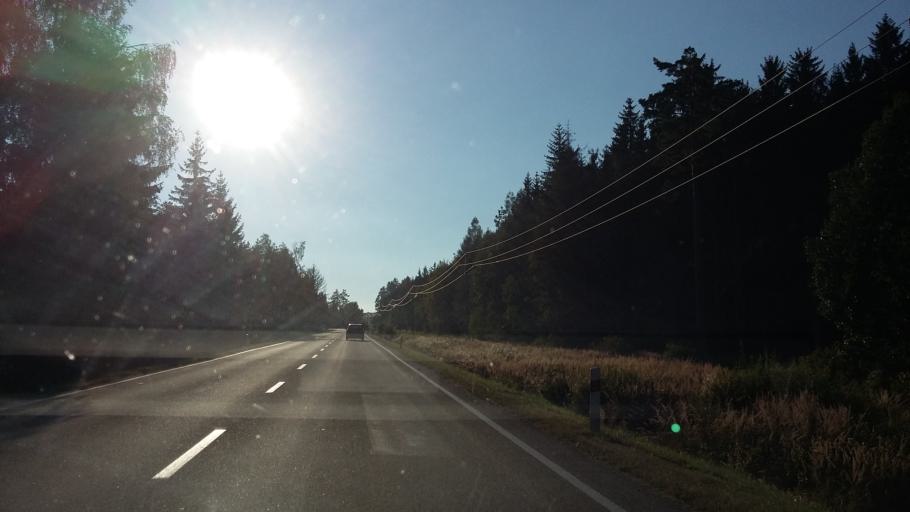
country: CZ
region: Vysocina
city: Kamenice
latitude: 49.4013
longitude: 15.8139
